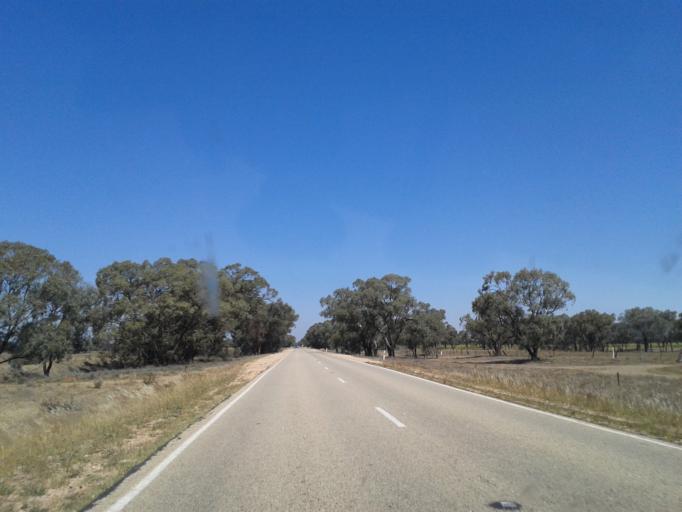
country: AU
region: Victoria
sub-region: Swan Hill
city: Swan Hill
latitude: -35.0125
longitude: 143.3105
